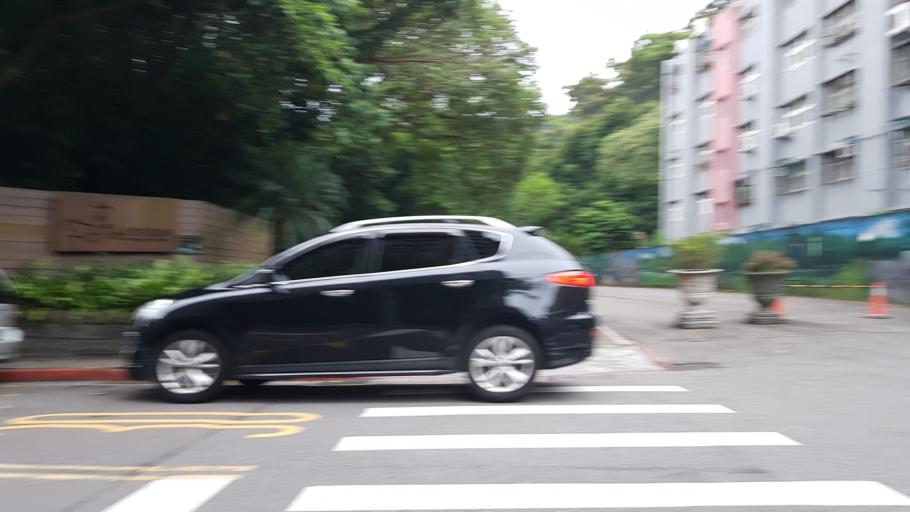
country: TW
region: Taipei
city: Taipei
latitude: 25.0171
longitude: 121.5570
